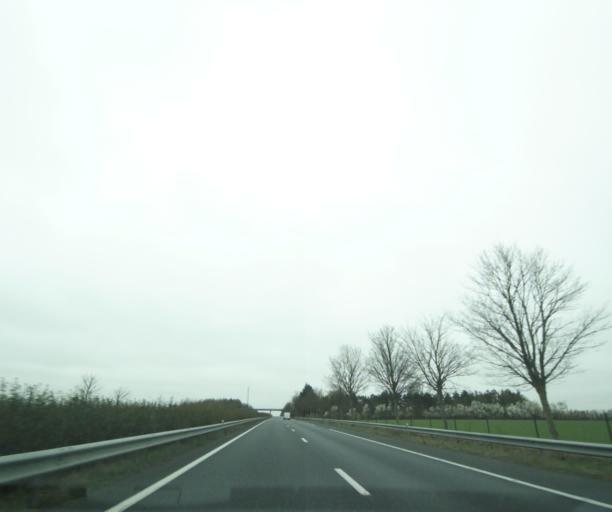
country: FR
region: Centre
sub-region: Departement de l'Indre
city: Vatan
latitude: 46.9979
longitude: 1.7759
